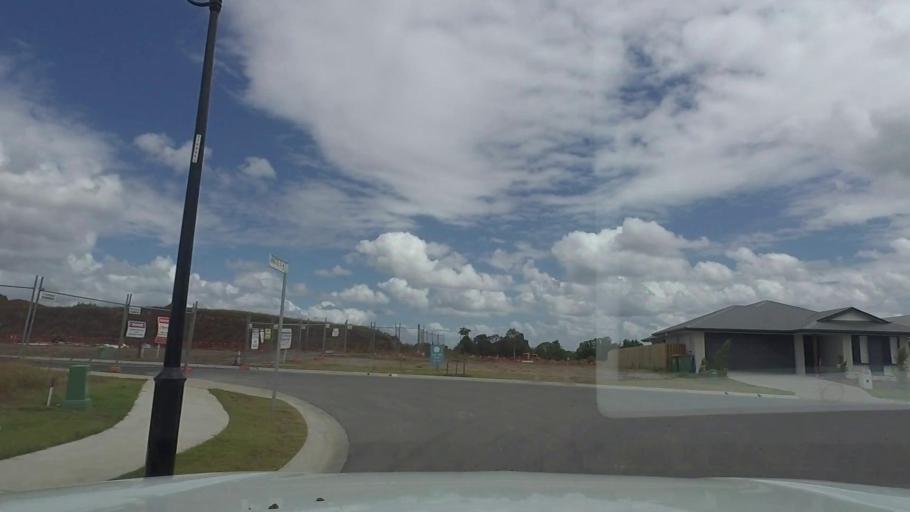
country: AU
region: Queensland
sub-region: Logan
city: Logan Reserve
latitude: -27.7193
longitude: 153.1162
